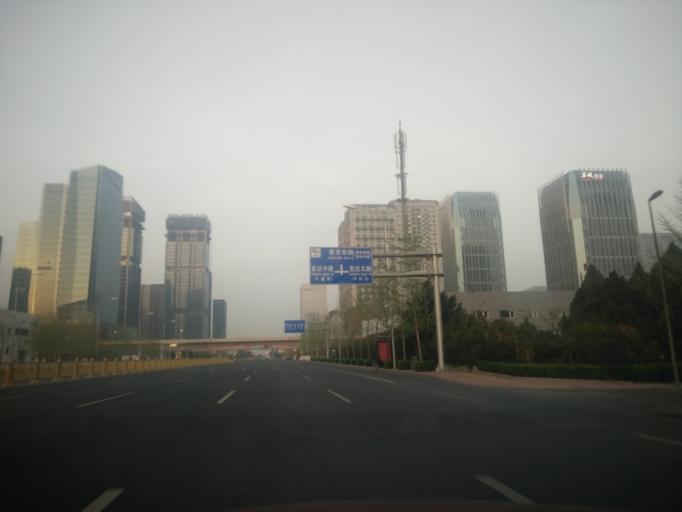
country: CN
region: Beijing
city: Jiugong
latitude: 39.7942
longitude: 116.5089
